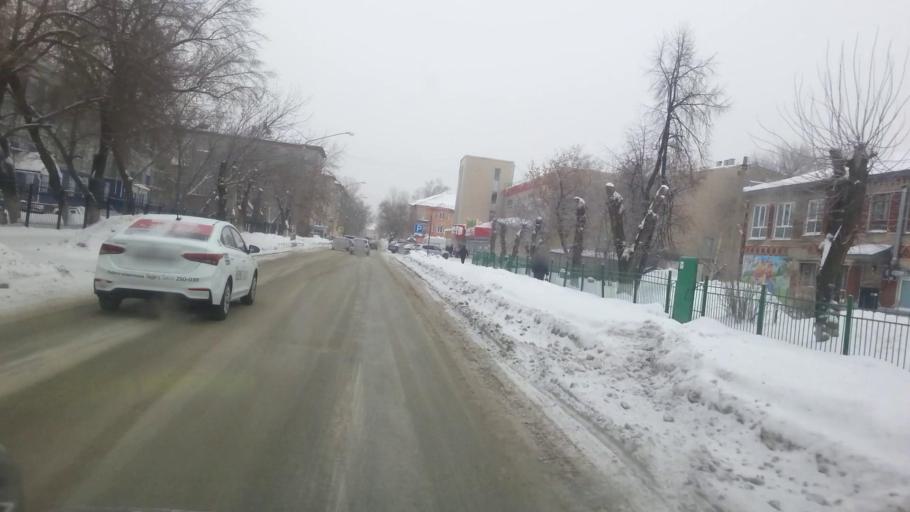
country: RU
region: Altai Krai
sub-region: Gorod Barnaulskiy
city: Barnaul
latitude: 53.3793
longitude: 83.7222
